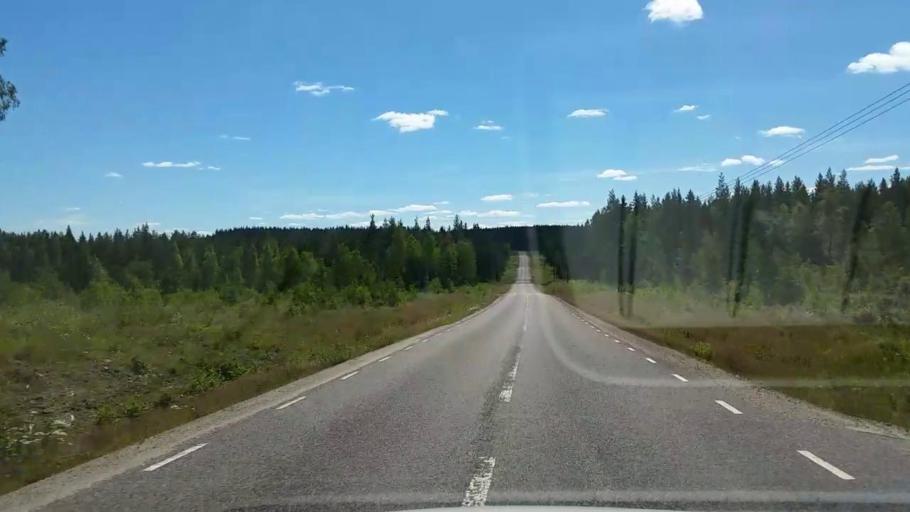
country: SE
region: Gaevleborg
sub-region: Ovanakers Kommun
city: Edsbyn
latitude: 61.5375
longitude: 15.6811
